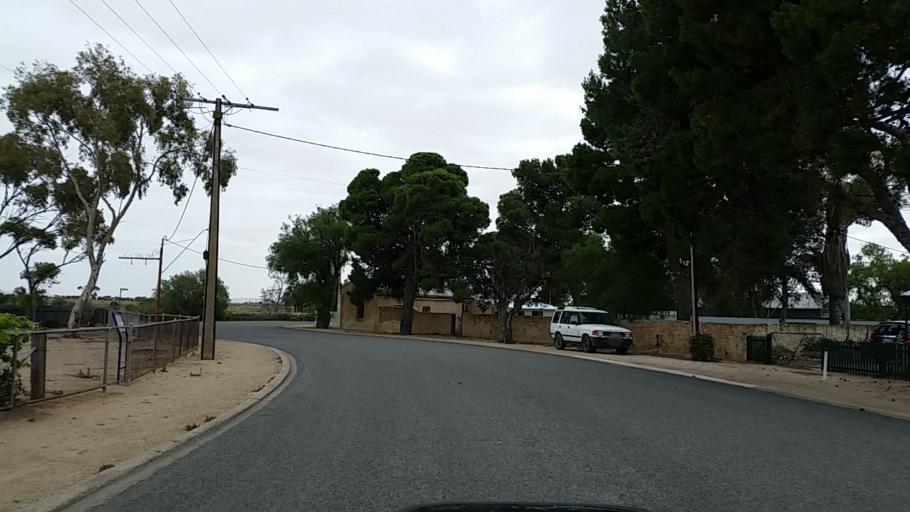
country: AU
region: South Australia
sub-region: Wakefield
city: Balaklava
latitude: -34.1842
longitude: 138.1472
